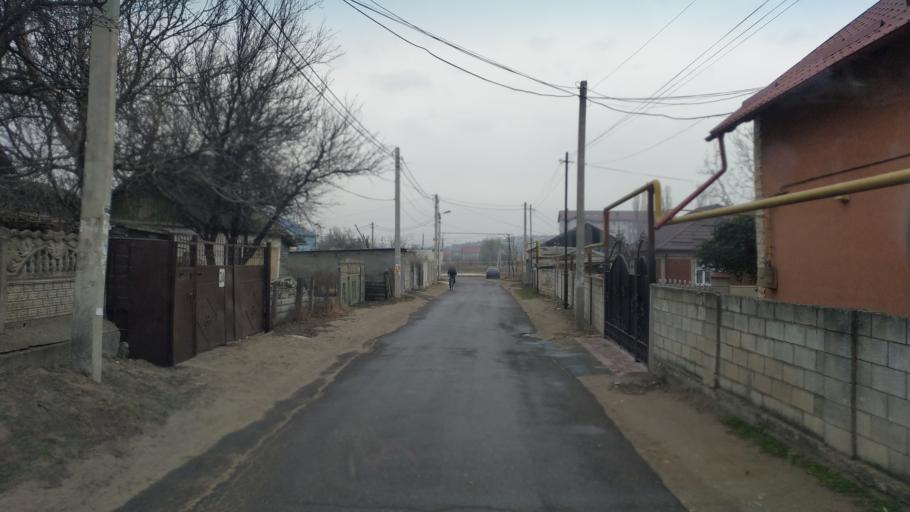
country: MD
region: Chisinau
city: Singera
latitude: 46.9149
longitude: 28.9719
